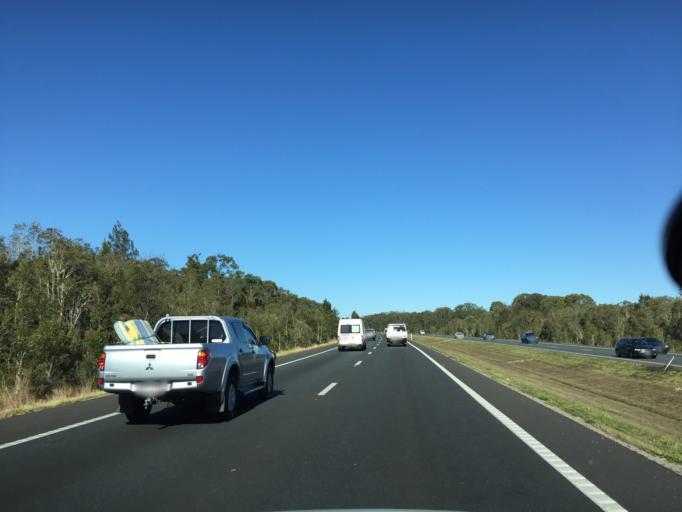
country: AU
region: Queensland
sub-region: Sunshine Coast
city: Little Mountain
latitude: -26.8682
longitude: 153.0119
